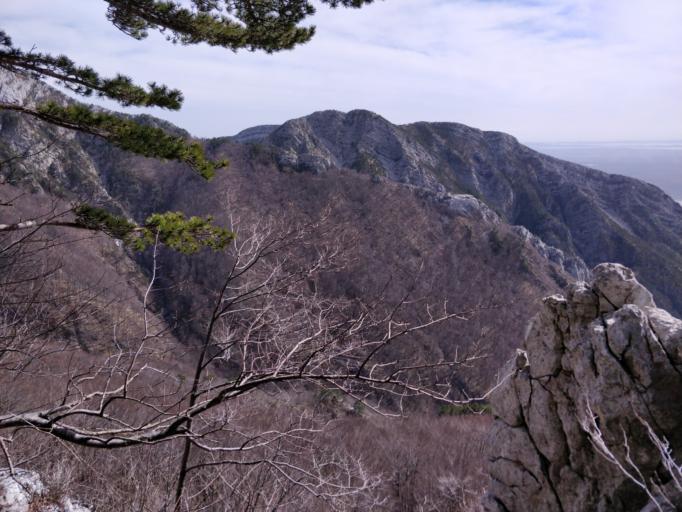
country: HR
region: Zadarska
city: Starigrad
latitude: 44.3337
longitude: 15.5433
